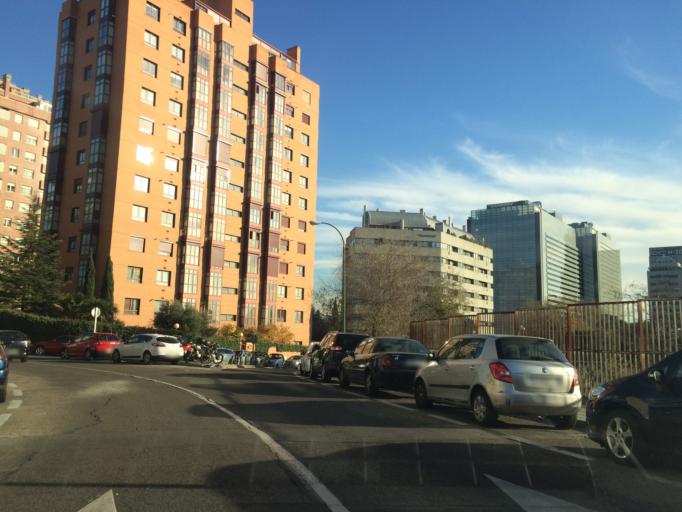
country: ES
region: Madrid
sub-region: Provincia de Madrid
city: Pinar de Chamartin
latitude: 40.4756
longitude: -3.6731
